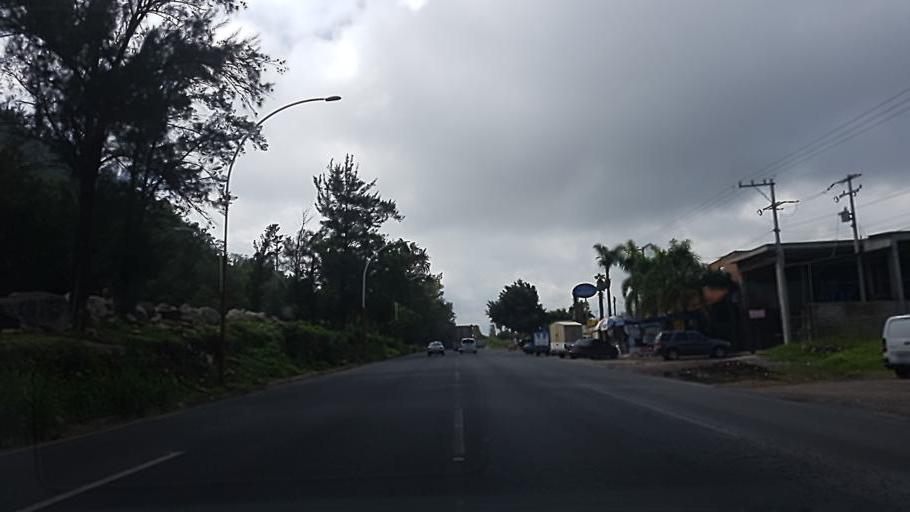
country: MX
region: Nayarit
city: Tepic
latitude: 21.5053
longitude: -104.9207
